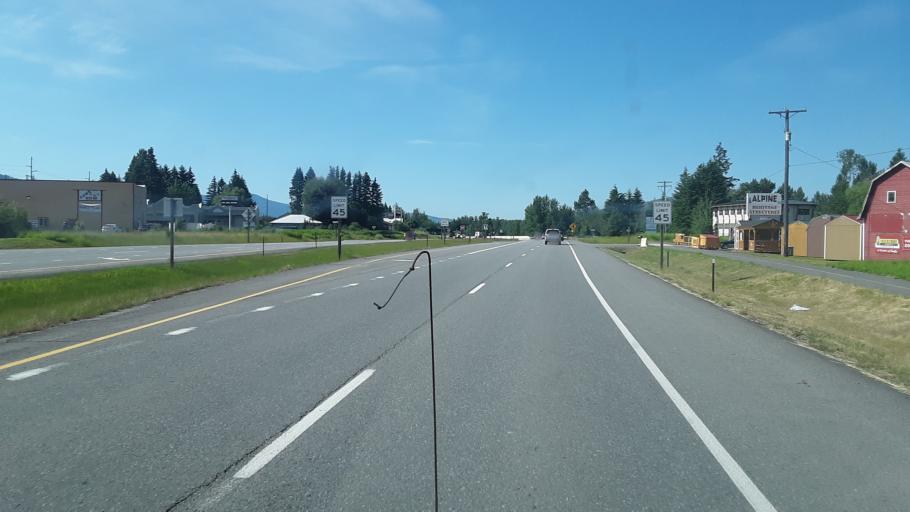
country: US
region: Idaho
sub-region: Bonner County
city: Ponderay
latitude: 48.3007
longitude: -116.5471
